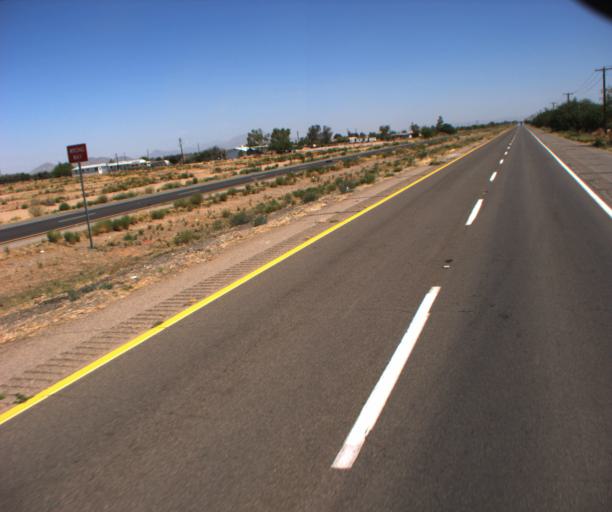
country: US
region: Arizona
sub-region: Pinal County
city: Maricopa
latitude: 32.9017
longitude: -112.0493
